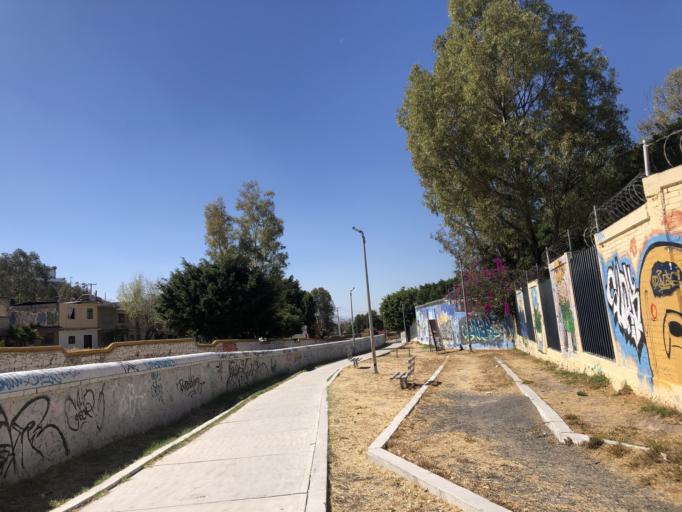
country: MX
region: Queretaro
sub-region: Queretaro
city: Santiago de Queretaro
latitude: 20.6135
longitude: -100.3746
